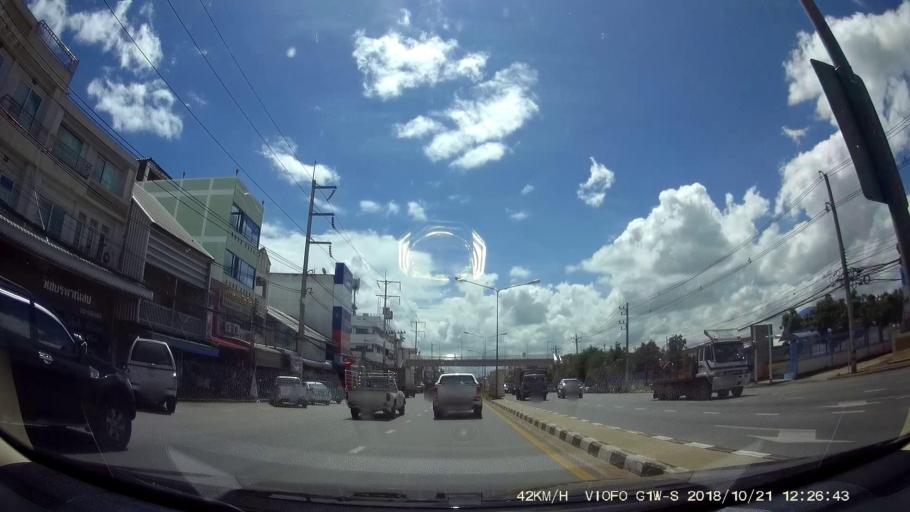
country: TH
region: Nakhon Ratchasima
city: Dan Khun Thot
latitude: 15.2085
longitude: 101.7671
